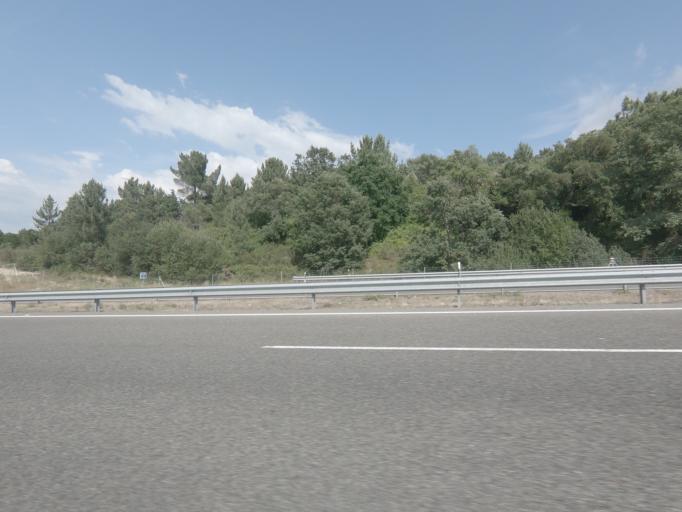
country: ES
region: Galicia
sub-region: Provincia de Ourense
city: Taboadela
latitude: 42.2783
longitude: -7.8726
